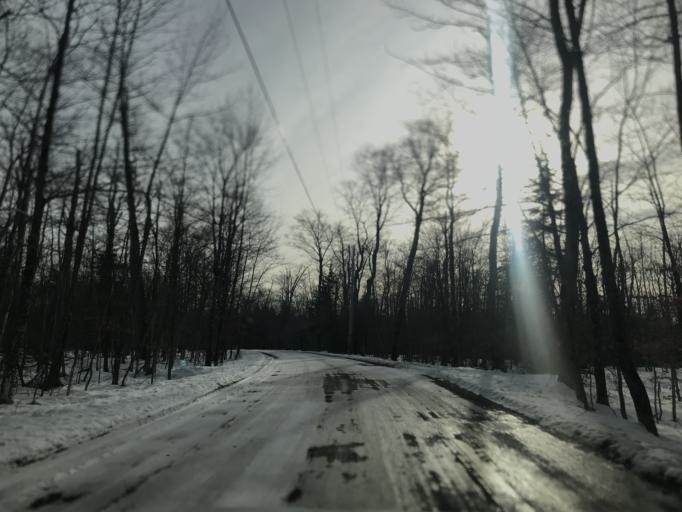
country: US
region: Wisconsin
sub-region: Door County
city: Sturgeon Bay
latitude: 45.1449
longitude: -87.0540
